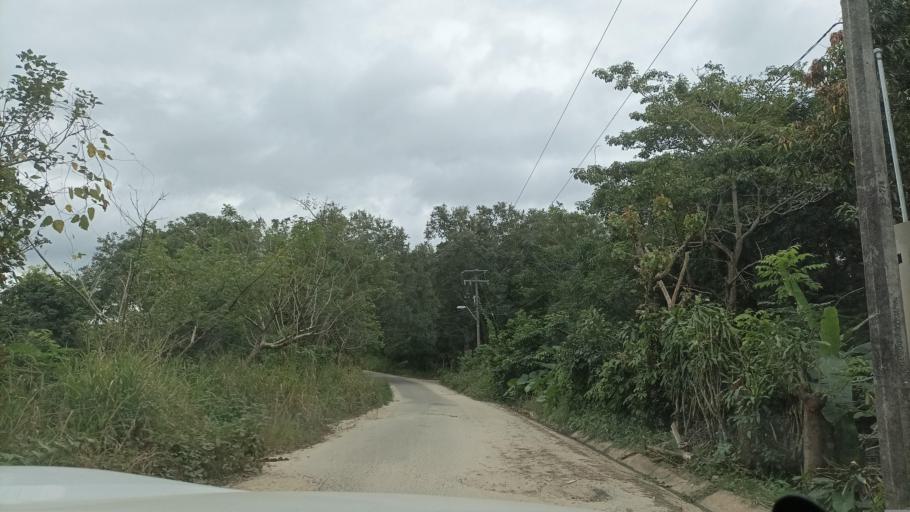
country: MX
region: Veracruz
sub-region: Cosoleacaque
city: Coacotla
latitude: 17.9480
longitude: -94.7100
